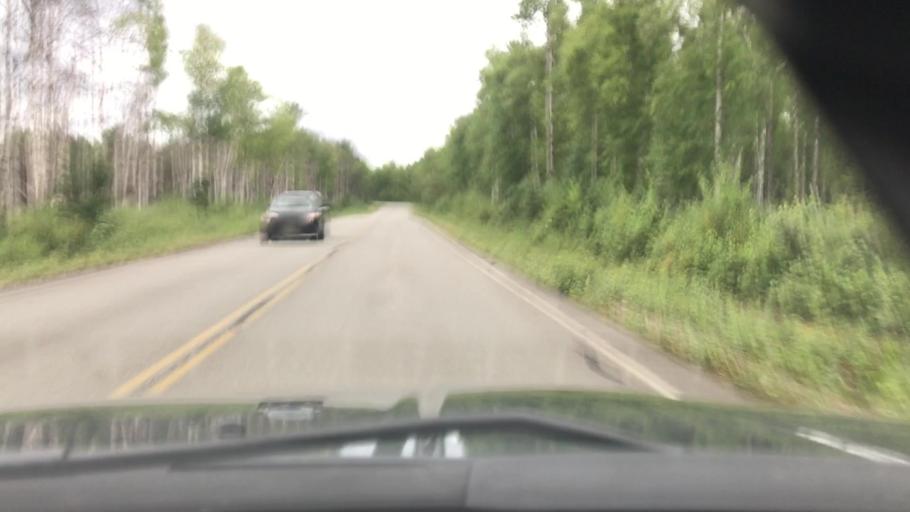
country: US
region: Alaska
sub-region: Matanuska-Susitna Borough
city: Willow
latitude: 61.7650
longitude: -150.1258
